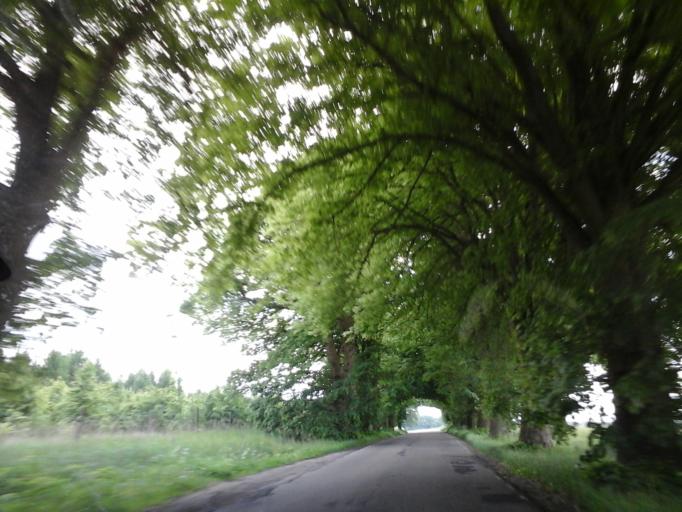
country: PL
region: West Pomeranian Voivodeship
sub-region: Powiat drawski
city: Kalisz Pomorski
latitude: 53.2522
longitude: 15.8411
